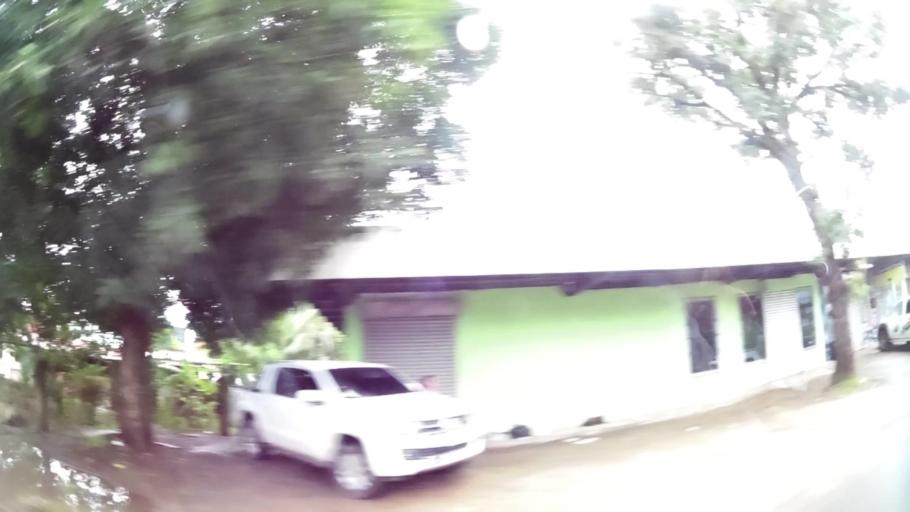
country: PA
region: Veraguas
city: Santiago de Veraguas
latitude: 8.1062
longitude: -80.9750
